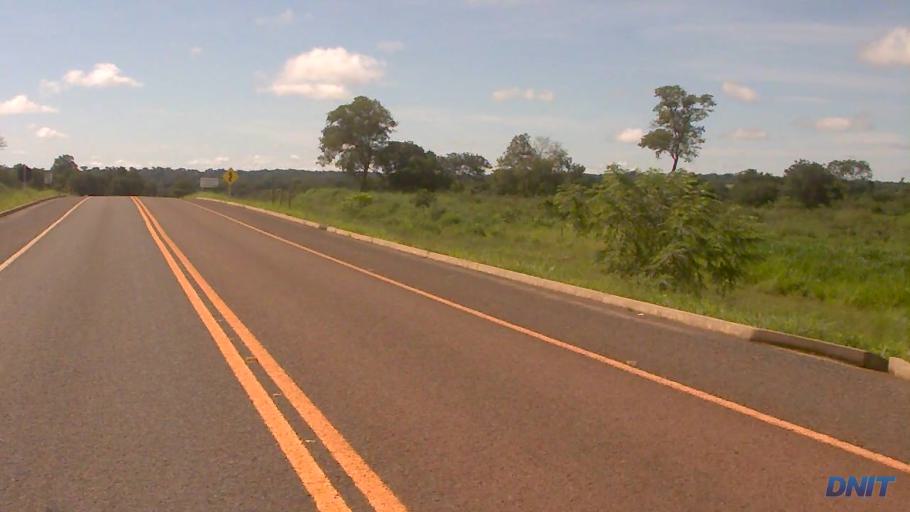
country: BR
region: Goias
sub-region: Sao Miguel Do Araguaia
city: Sao Miguel do Araguaia
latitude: -13.2867
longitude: -50.1813
